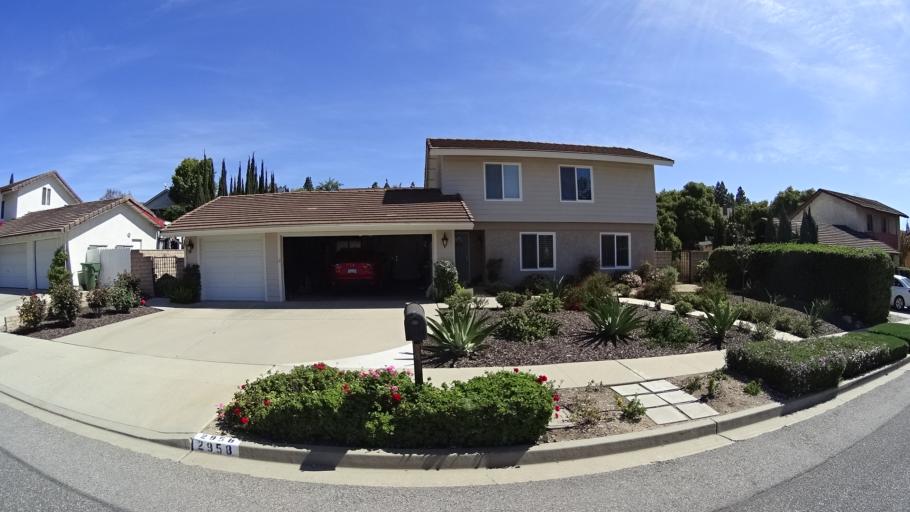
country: US
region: California
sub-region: Ventura County
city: Thousand Oaks
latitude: 34.2196
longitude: -118.8568
